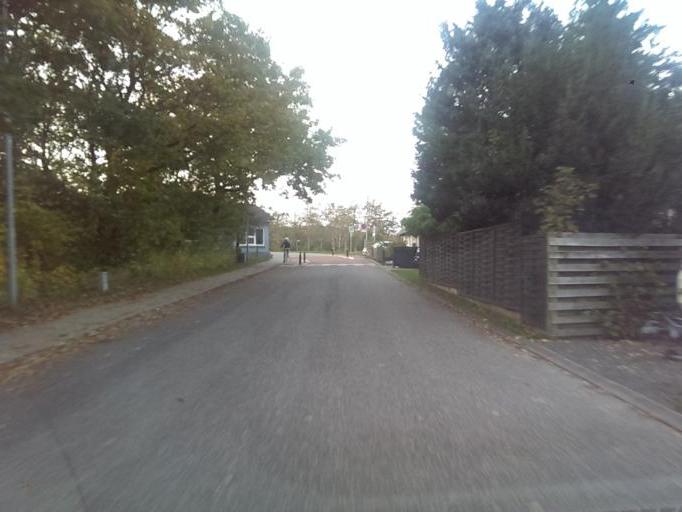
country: DK
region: South Denmark
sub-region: Esbjerg Kommune
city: Tjaereborg
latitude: 55.4651
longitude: 8.5823
